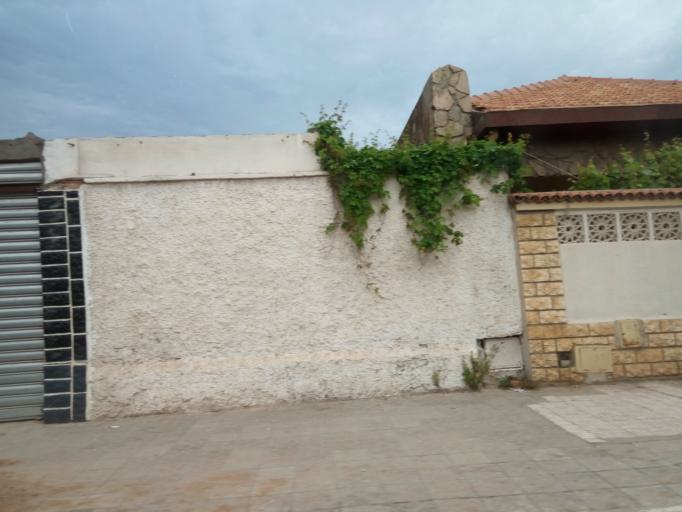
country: DZ
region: Tipaza
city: Cheraga
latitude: 36.8159
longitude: 3.0022
